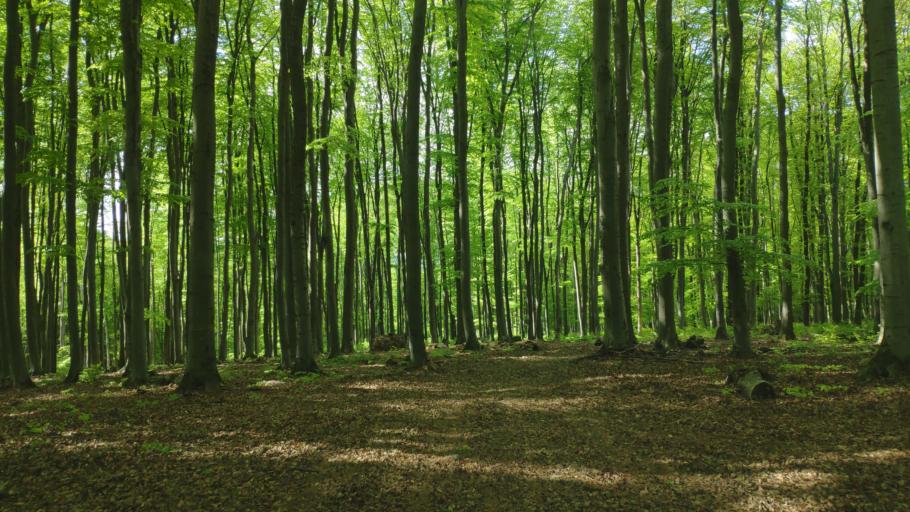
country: SK
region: Kosicky
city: Kosice
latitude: 48.6683
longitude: 21.4479
